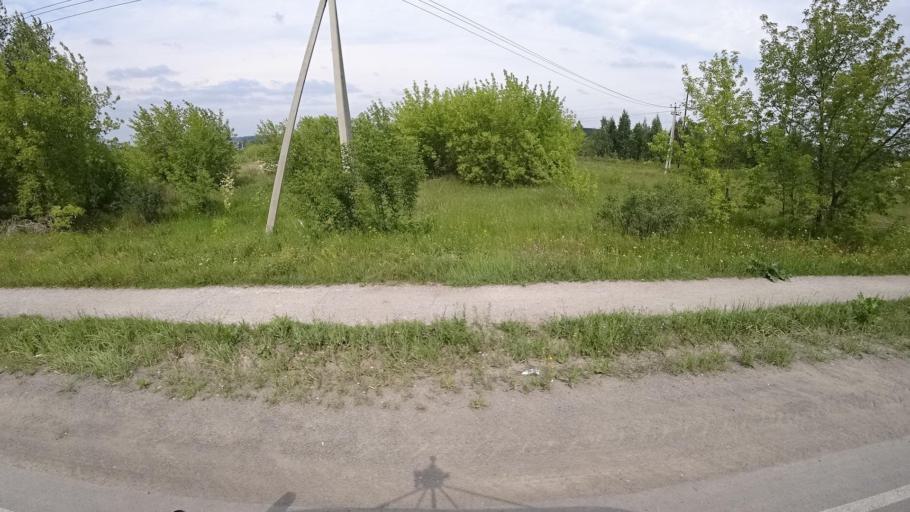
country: RU
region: Sverdlovsk
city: Kamyshlov
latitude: 56.8577
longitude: 62.7244
